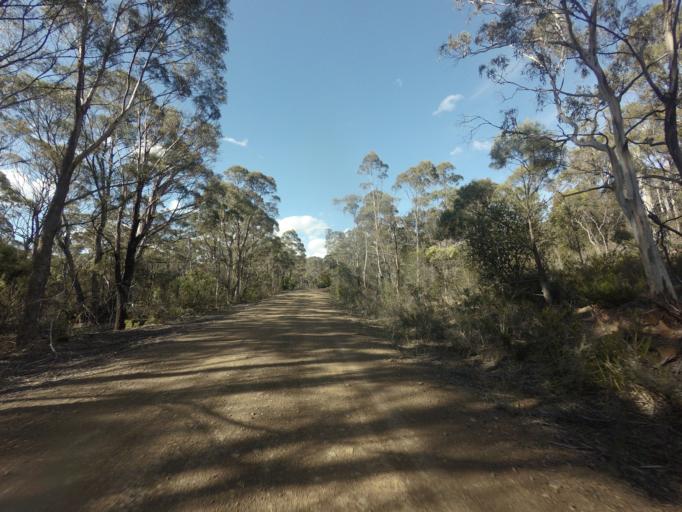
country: AU
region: Tasmania
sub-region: Break O'Day
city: St Helens
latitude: -41.8577
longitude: 148.0243
